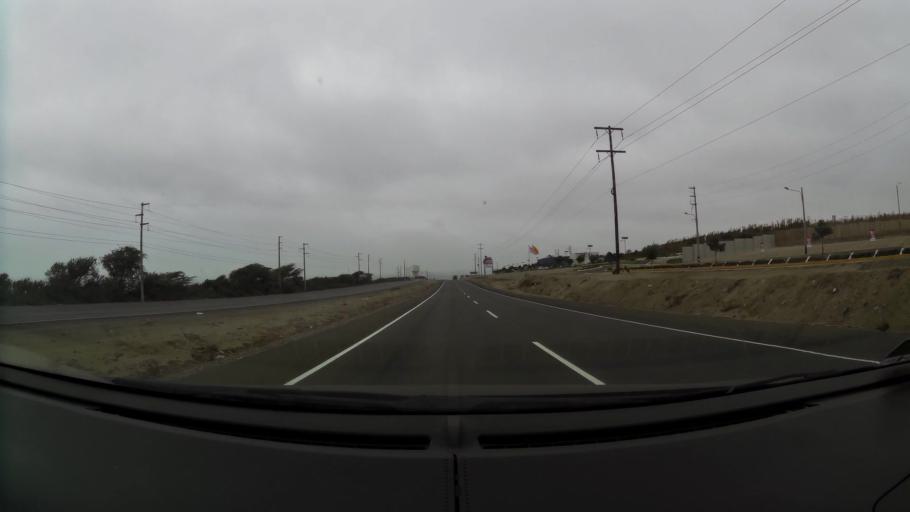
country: PE
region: La Libertad
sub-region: Provincia de Trujillo
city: Salaverry
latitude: -8.1938
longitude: -78.9723
